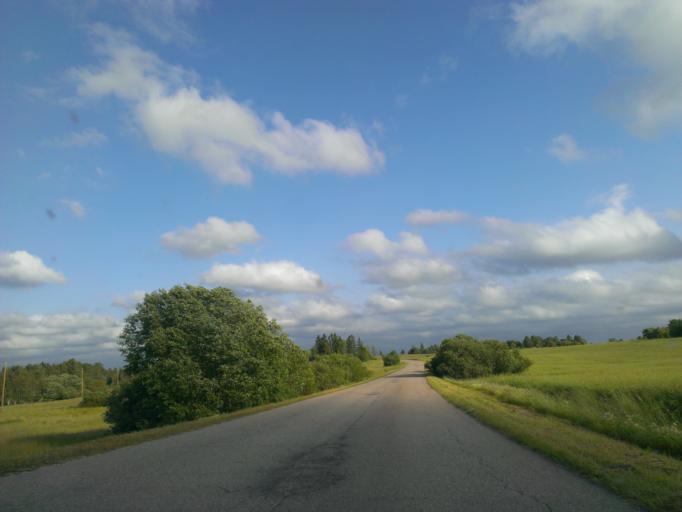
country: LV
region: Aizpute
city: Aizpute
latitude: 56.7628
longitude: 21.5413
